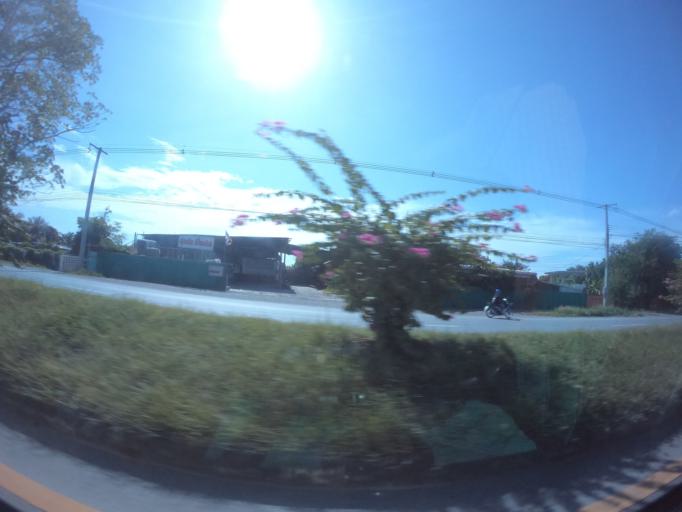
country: TH
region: Nakhon Nayok
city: Ban Na
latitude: 14.2213
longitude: 101.0698
